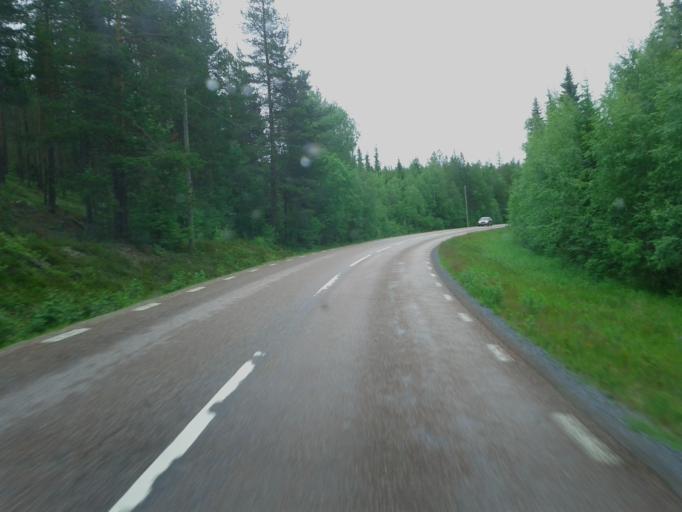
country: NO
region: Hedmark
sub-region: Trysil
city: Innbygda
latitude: 61.8295
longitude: 12.8638
